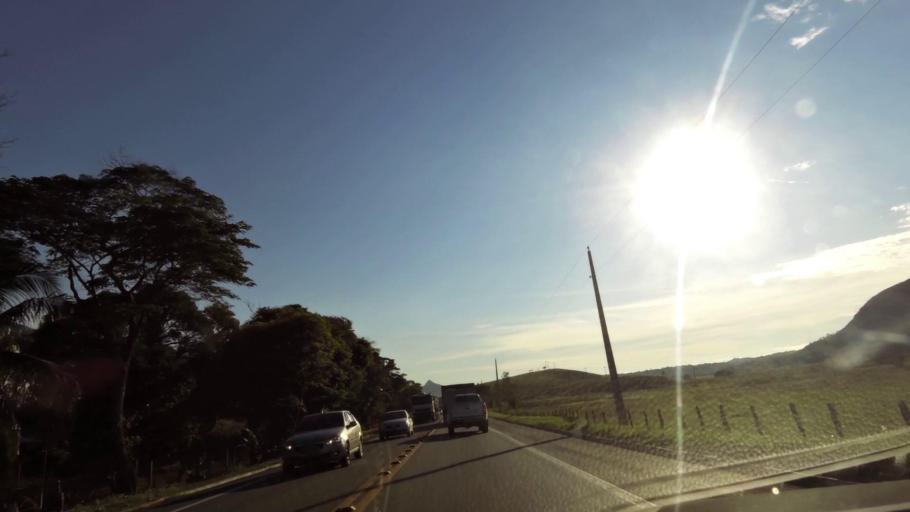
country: BR
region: Espirito Santo
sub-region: Guarapari
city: Guarapari
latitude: -20.6127
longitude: -40.5118
